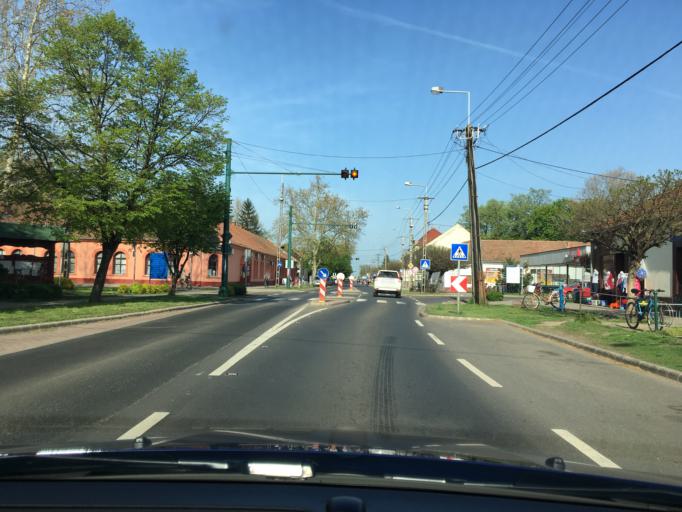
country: HU
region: Bekes
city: Csorvas
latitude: 46.6334
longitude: 20.8289
